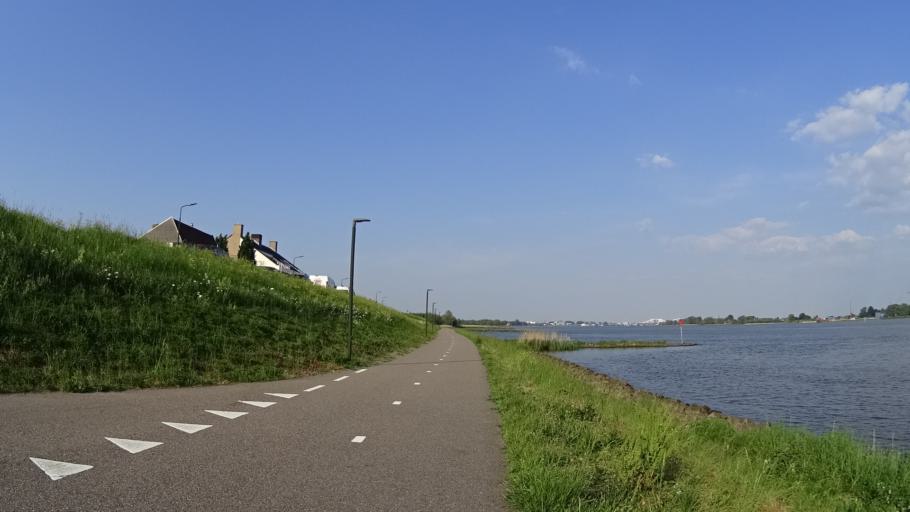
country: NL
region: South Holland
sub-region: Gemeente Hardinxveld-Giessendam
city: Boven-Hardinxveld
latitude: 51.8221
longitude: 4.8909
